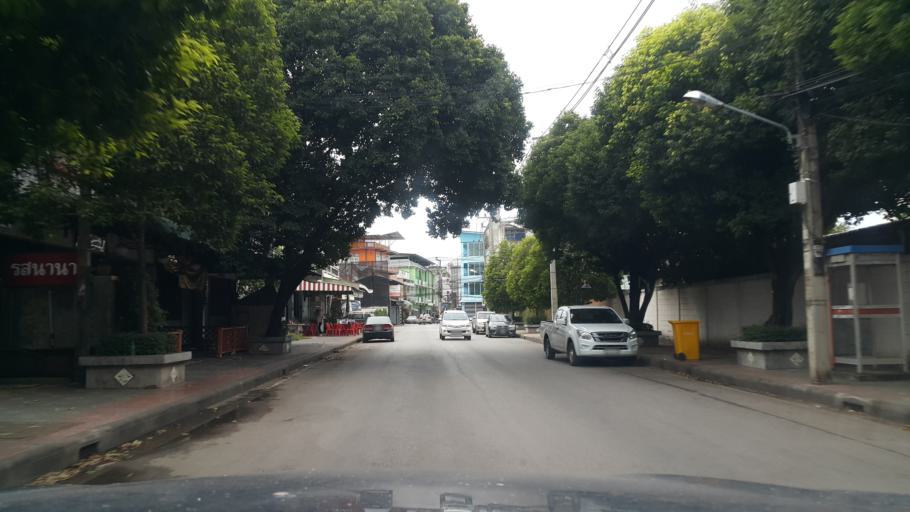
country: TH
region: Lampang
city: Lampang
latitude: 18.2862
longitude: 99.4961
